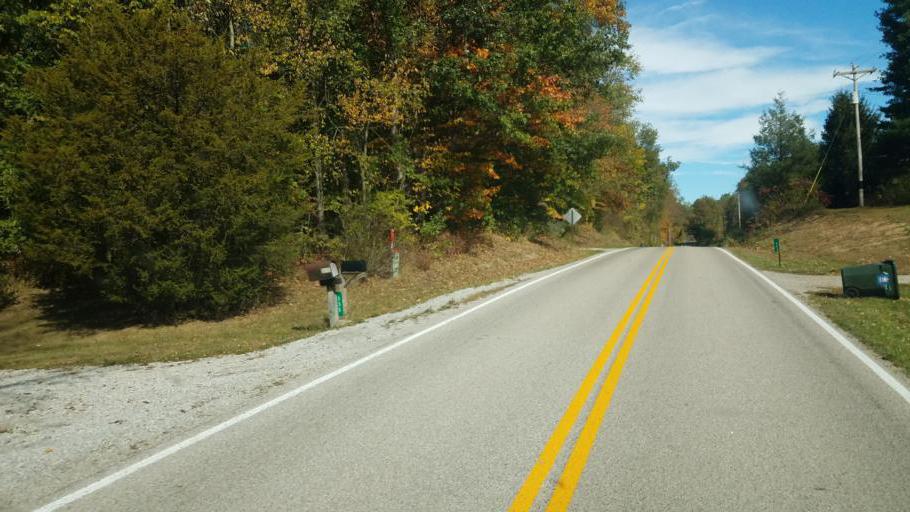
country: US
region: Ohio
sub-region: Huron County
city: New London
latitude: 41.1538
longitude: -82.4588
